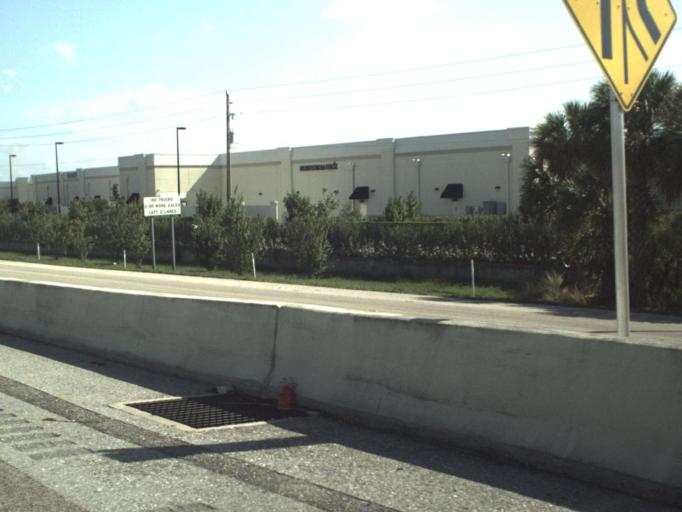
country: US
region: Florida
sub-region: Palm Beach County
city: Schall Circle
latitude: 26.7217
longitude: -80.0908
